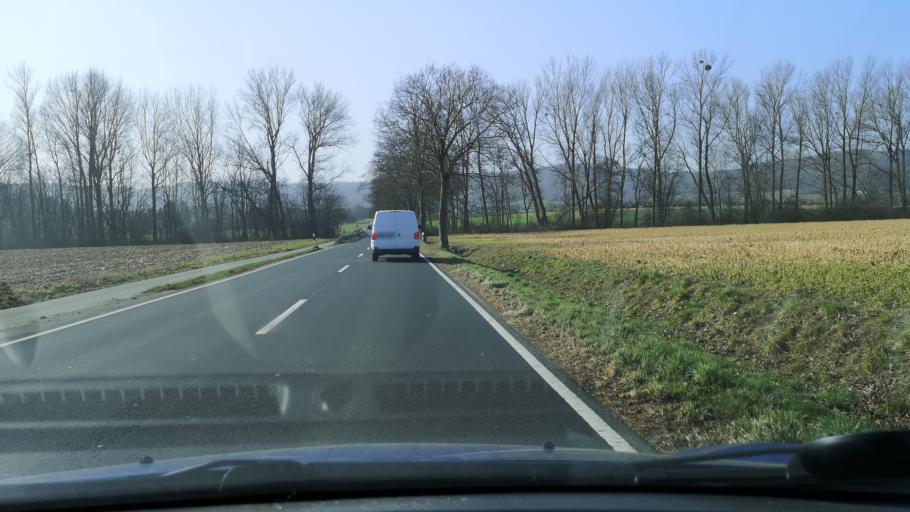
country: DE
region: Lower Saxony
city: Salzhemmendorf
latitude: 52.0786
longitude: 9.5938
